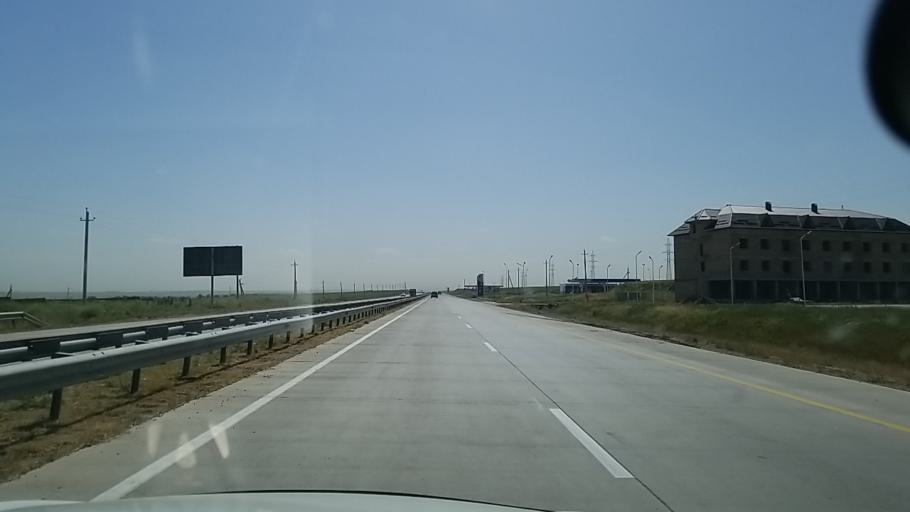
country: KZ
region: Ongtustik Qazaqstan
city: Shymkent
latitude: 42.4504
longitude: 69.6419
